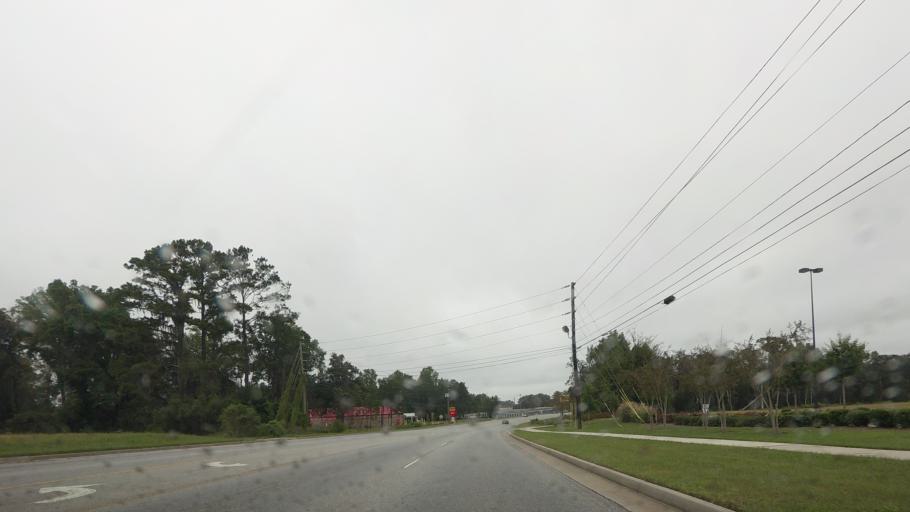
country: US
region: Georgia
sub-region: Lowndes County
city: Remerton
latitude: 30.8305
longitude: -83.3200
